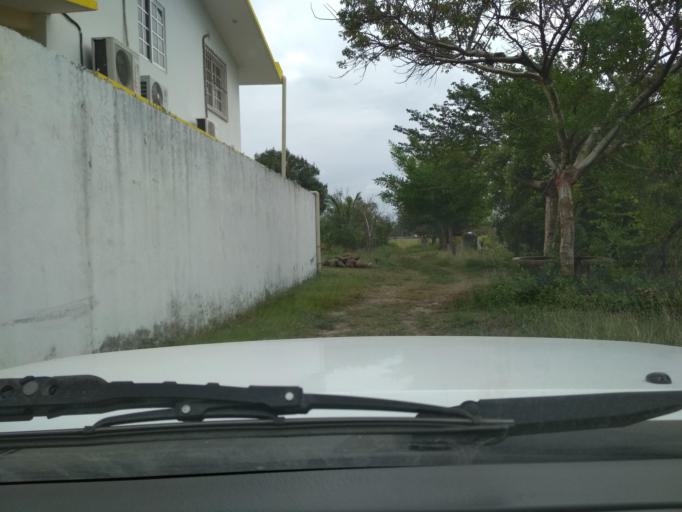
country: MX
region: Veracruz
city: El Tejar
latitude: 19.0625
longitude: -96.1388
